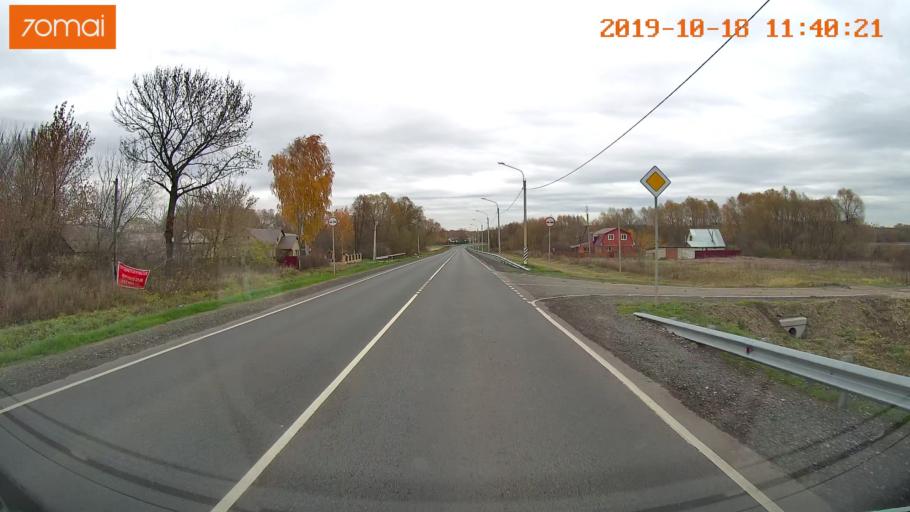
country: RU
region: Rjazan
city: Oktyabr'skiy
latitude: 54.1792
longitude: 38.8896
